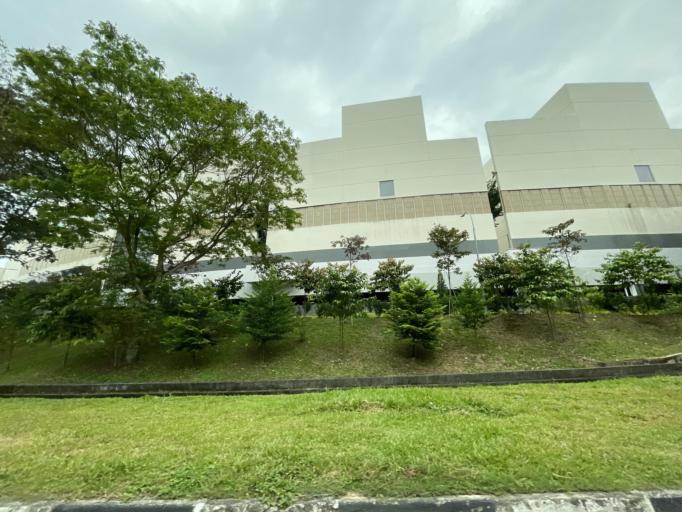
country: SG
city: Singapore
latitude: 1.3029
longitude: 103.7726
